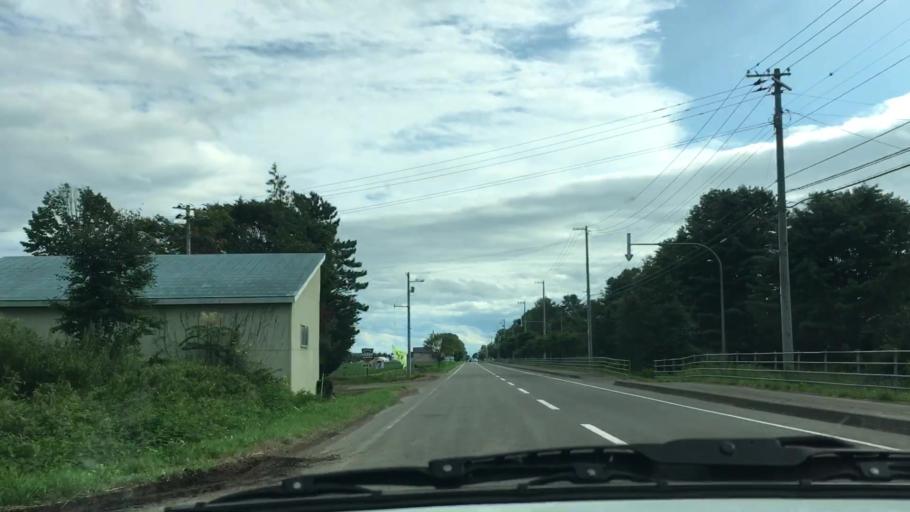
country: JP
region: Hokkaido
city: Otofuke
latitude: 43.2479
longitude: 143.2985
